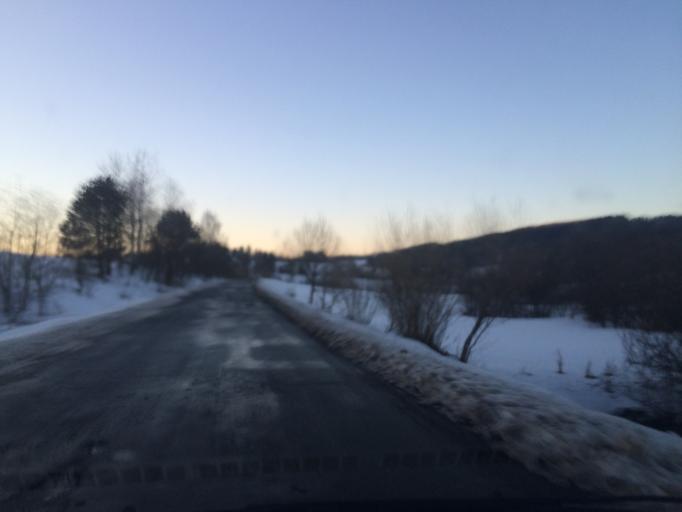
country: PL
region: Subcarpathian Voivodeship
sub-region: Powiat bieszczadzki
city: Ustrzyki Dolne
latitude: 49.3914
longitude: 22.6285
